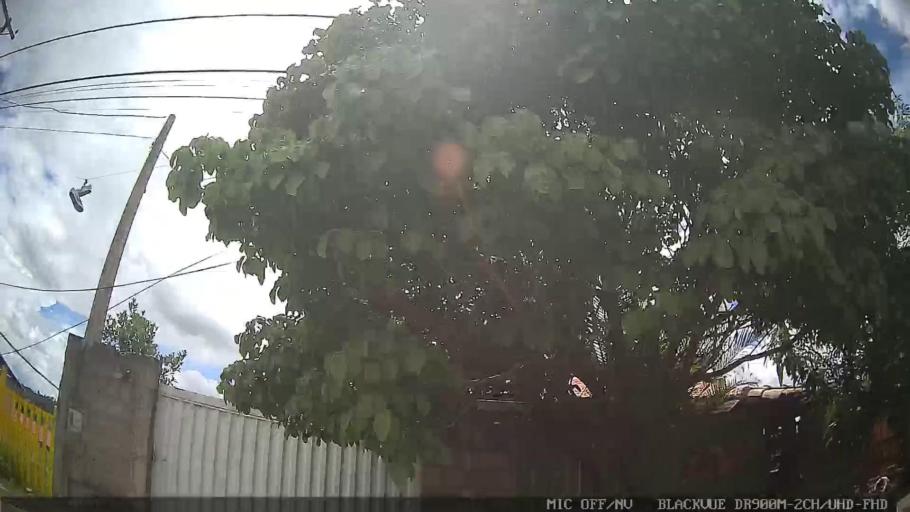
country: BR
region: Sao Paulo
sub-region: Jaguariuna
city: Jaguariuna
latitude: -22.7042
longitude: -46.9620
